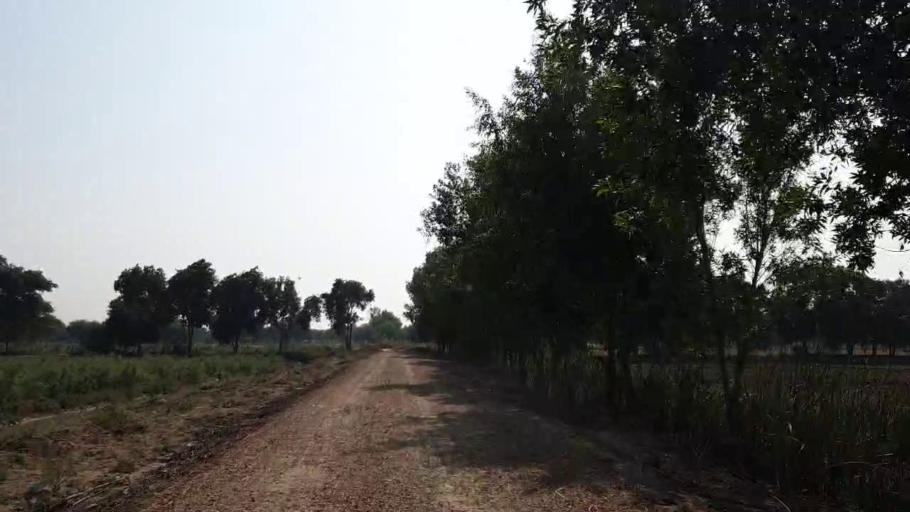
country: PK
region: Sindh
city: Tando Muhammad Khan
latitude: 25.0163
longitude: 68.4179
